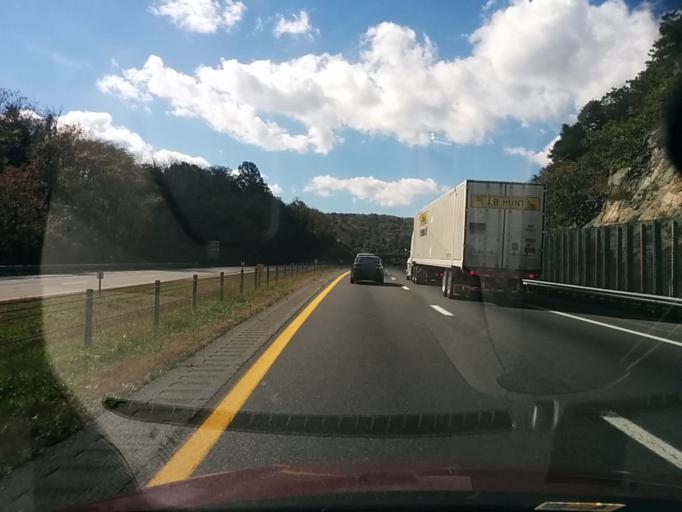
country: US
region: Virginia
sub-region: City of Waynesboro
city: Waynesboro
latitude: 38.0333
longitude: -78.8552
